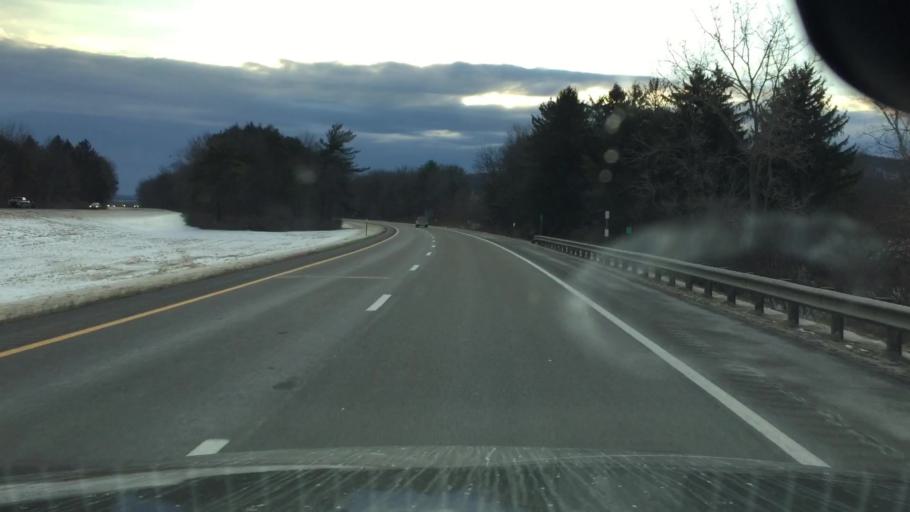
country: US
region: Pennsylvania
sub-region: Bradford County
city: South Waverly
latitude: 42.0021
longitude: -76.6215
